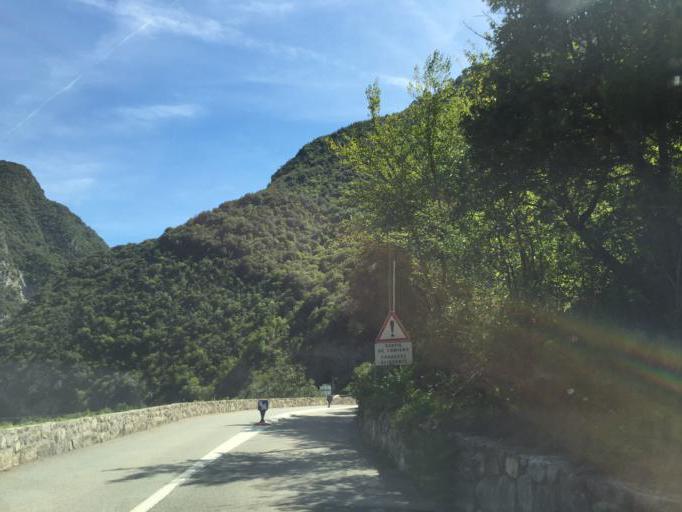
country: FR
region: Provence-Alpes-Cote d'Azur
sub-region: Departement des Alpes-Maritimes
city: Levens
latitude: 43.9238
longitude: 7.1862
